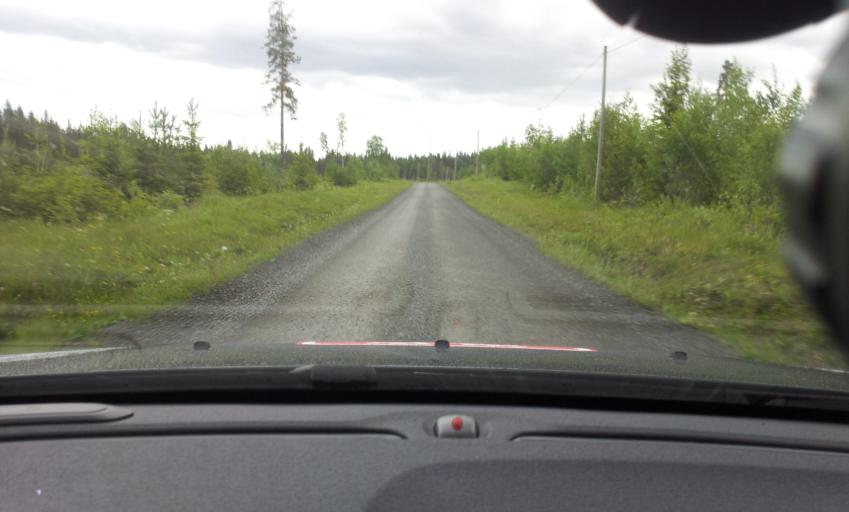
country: SE
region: Jaemtland
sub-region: OEstersunds Kommun
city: Brunflo
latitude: 63.1763
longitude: 14.9376
